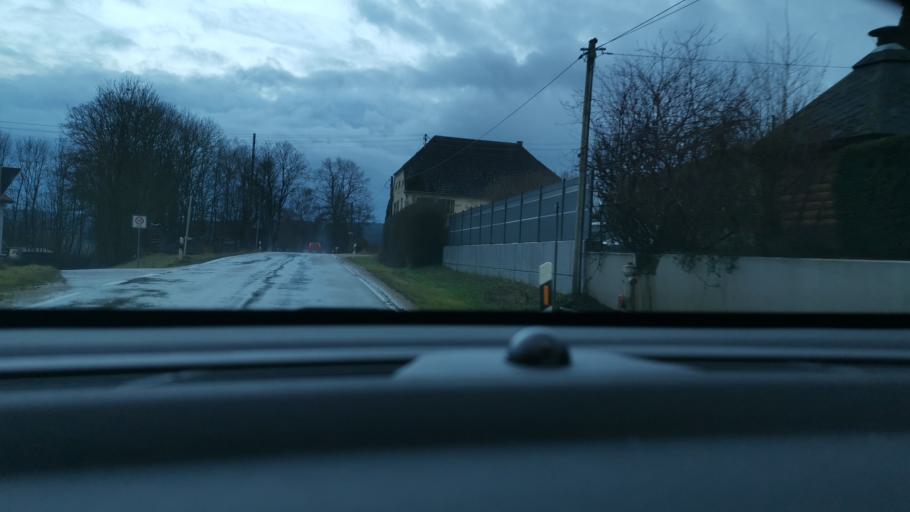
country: DE
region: Bavaria
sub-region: Swabia
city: Aindling
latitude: 48.5573
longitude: 10.9868
